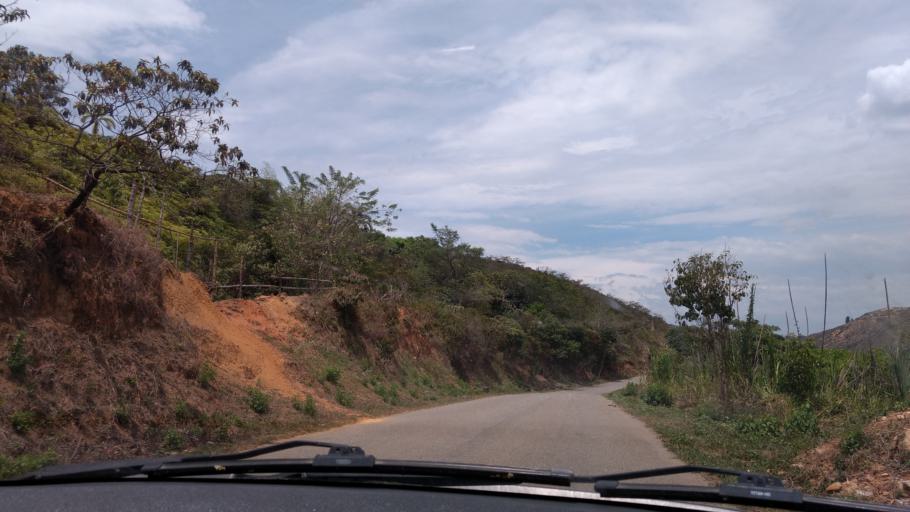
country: CO
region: Cauca
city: Buenos Aires
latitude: 3.0465
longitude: -76.6639
